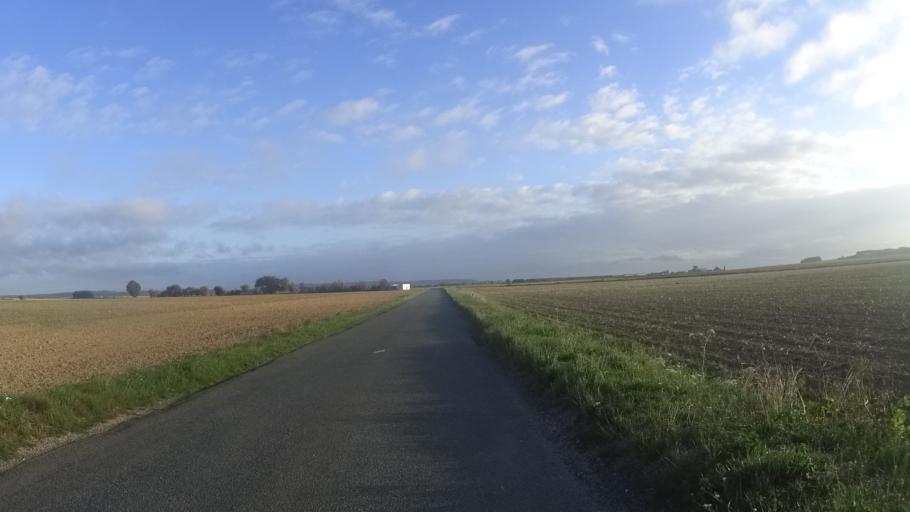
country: FR
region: Picardie
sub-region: Departement de l'Oise
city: Chamant
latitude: 49.1963
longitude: 2.6687
